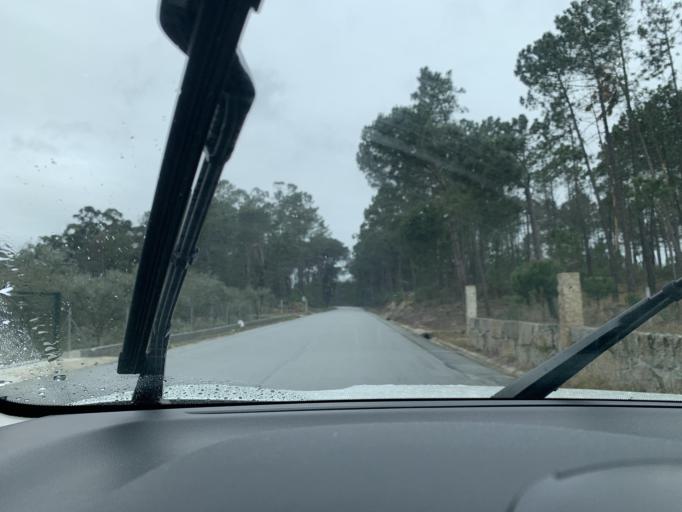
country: PT
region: Viseu
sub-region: Mangualde
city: Mangualde
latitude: 40.5971
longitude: -7.8228
